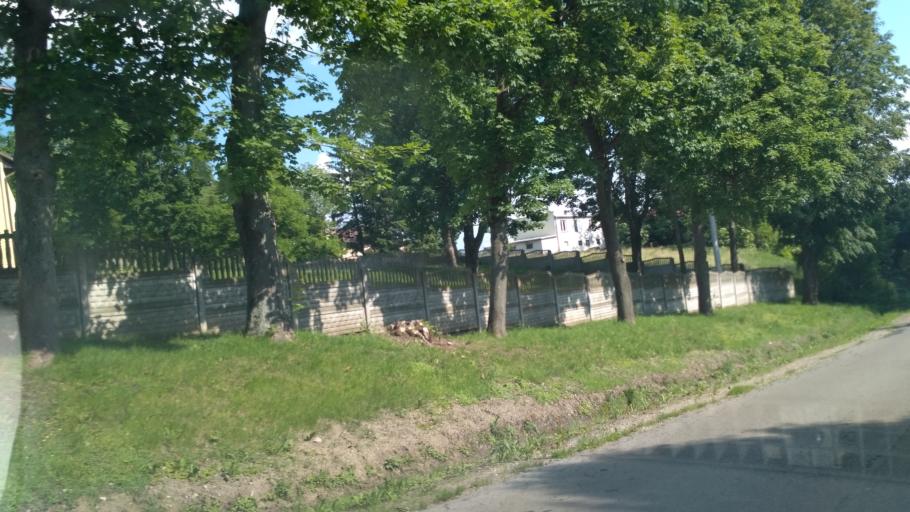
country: PL
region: Subcarpathian Voivodeship
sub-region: Powiat jaroslawski
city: Ostrow
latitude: 49.9400
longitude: 22.7394
